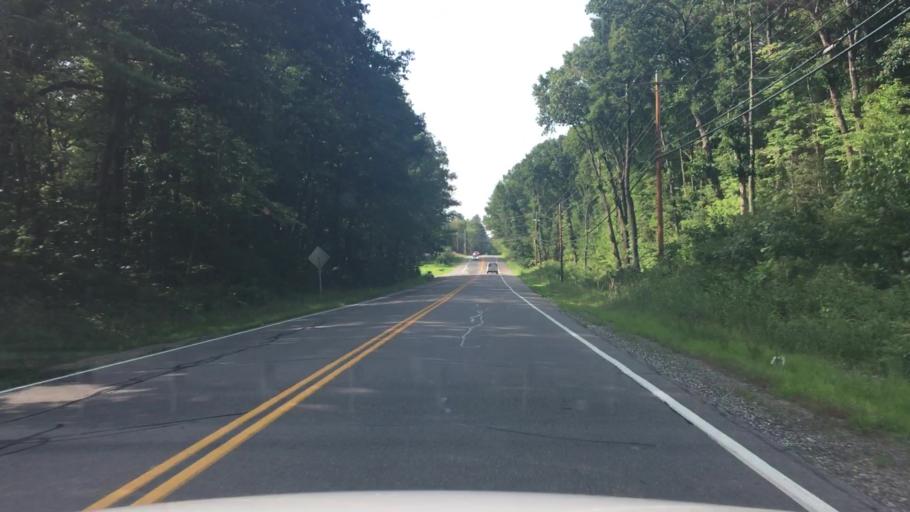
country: US
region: New Hampshire
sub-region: Rockingham County
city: Auburn
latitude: 42.9587
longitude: -71.3576
